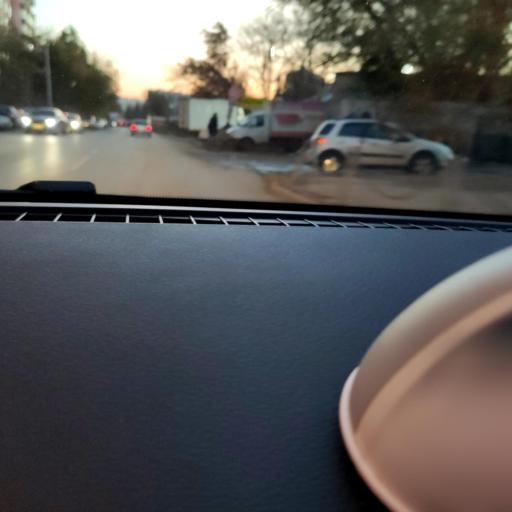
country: RU
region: Samara
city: Petra-Dubrava
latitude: 53.2395
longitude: 50.2754
